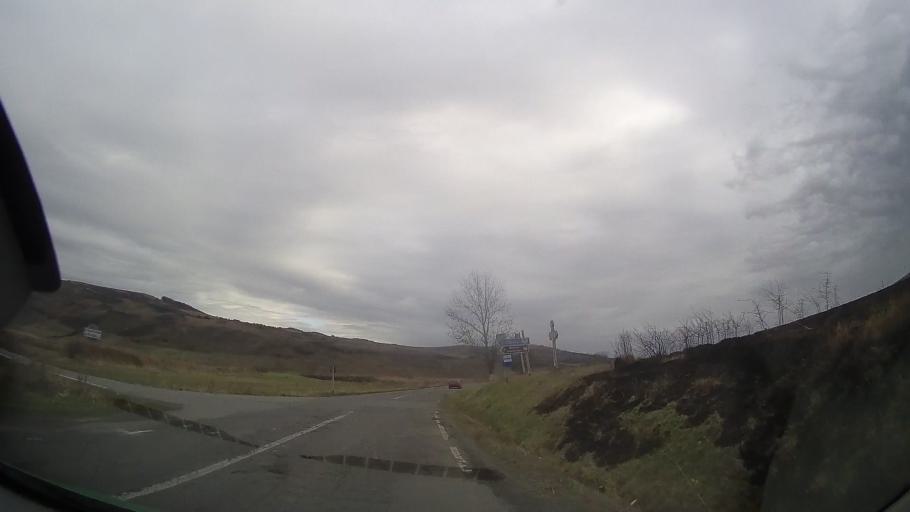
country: RO
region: Mures
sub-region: Comuna Faragau
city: Faragau
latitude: 46.7649
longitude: 24.5582
